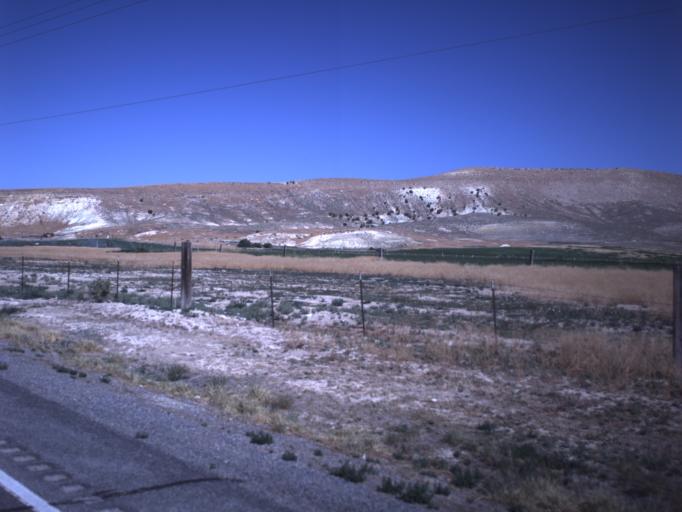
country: US
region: Utah
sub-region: Sanpete County
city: Gunnison
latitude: 39.1589
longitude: -111.7558
